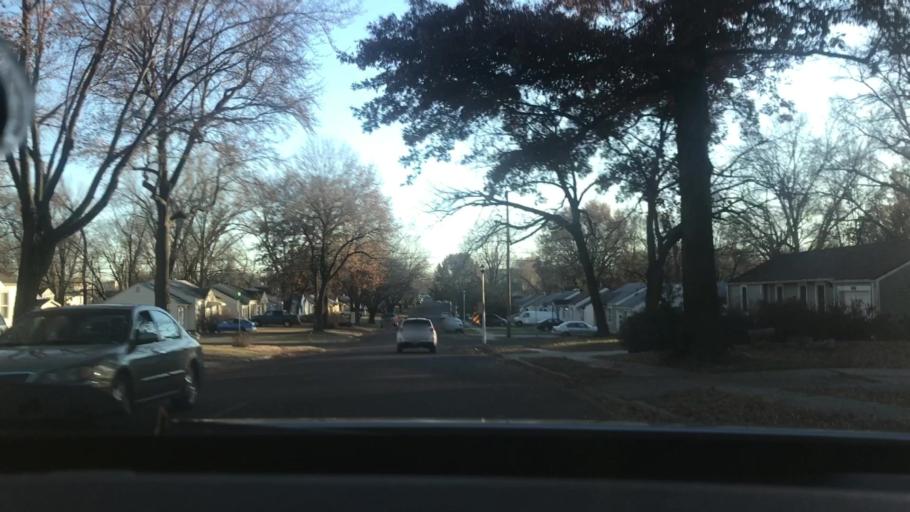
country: US
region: Kansas
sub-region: Johnson County
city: Overland Park
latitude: 38.9900
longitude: -94.6736
